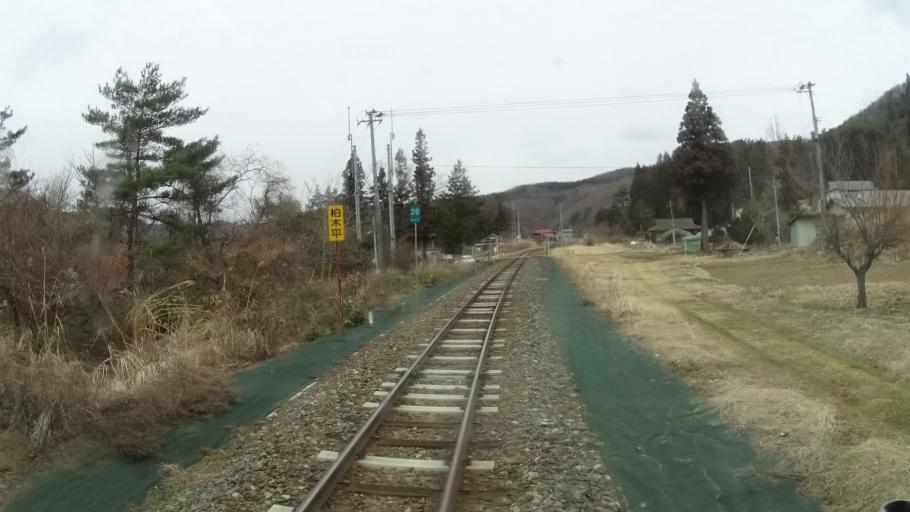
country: JP
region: Iwate
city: Tono
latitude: 39.3046
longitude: 141.3799
